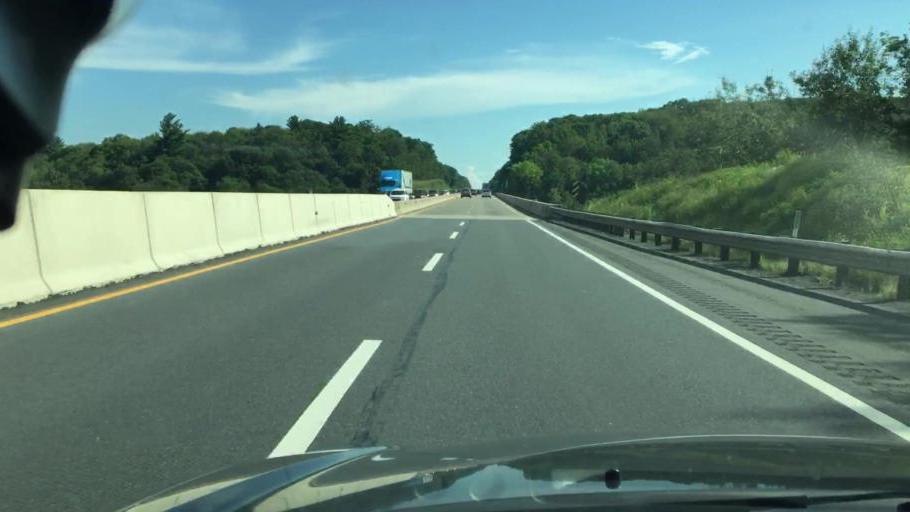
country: US
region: Pennsylvania
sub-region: Carbon County
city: Towamensing Trails
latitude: 41.0064
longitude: -75.6357
